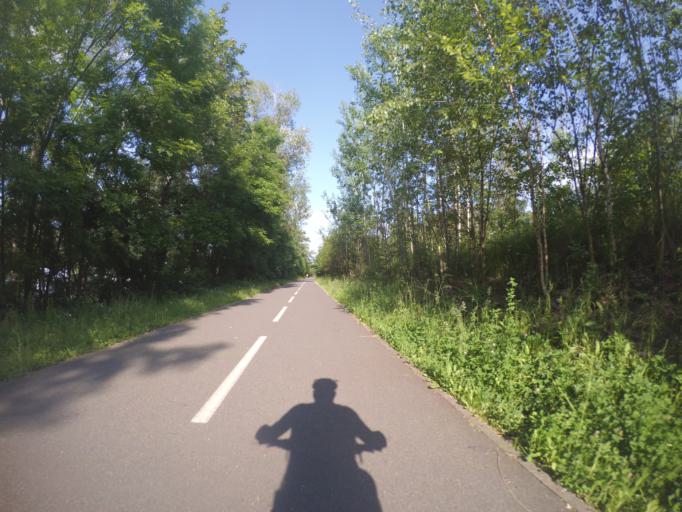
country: CZ
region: Praha
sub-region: Praha 9
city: Prosek
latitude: 50.1050
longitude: 14.5068
